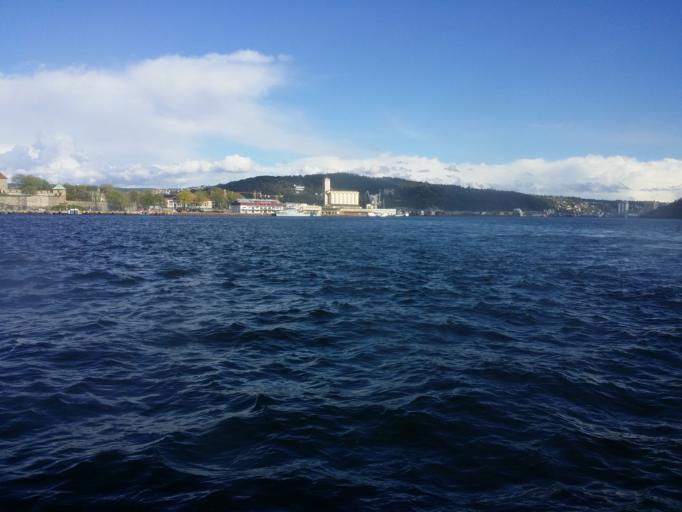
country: NO
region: Oslo
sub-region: Oslo
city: Oslo
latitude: 59.9058
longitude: 10.7265
